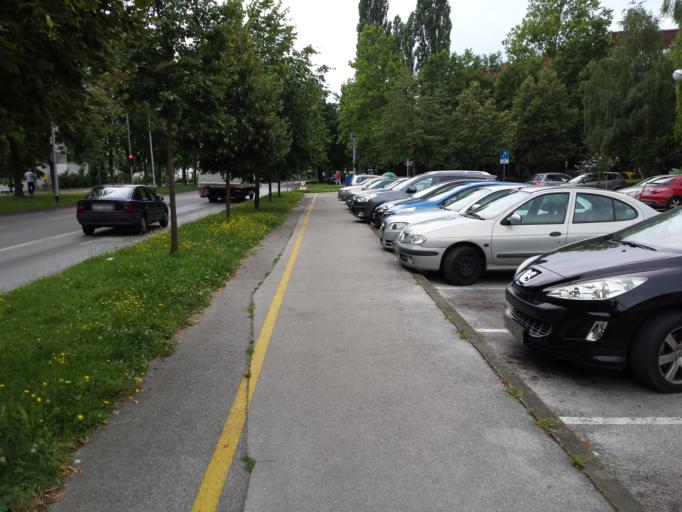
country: HR
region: Grad Zagreb
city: Jankomir
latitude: 45.7995
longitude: 15.9023
